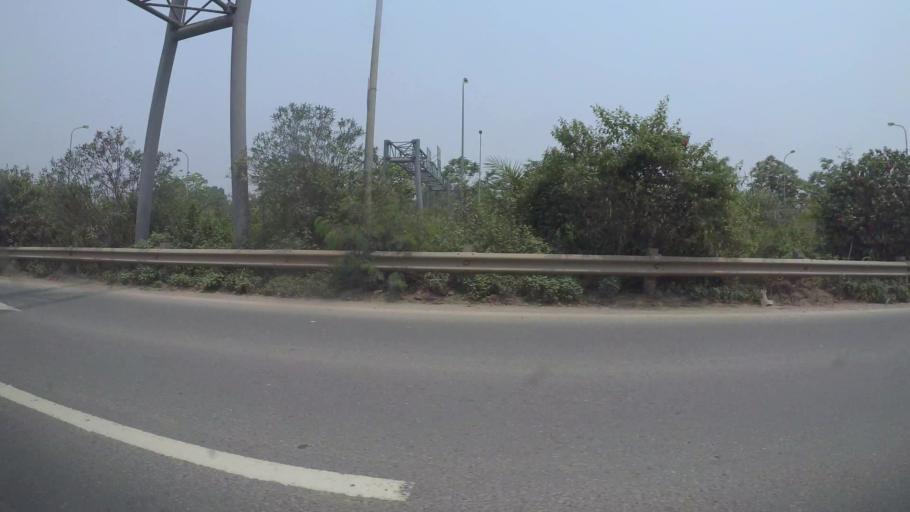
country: VN
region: Ha Noi
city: Lien Quan
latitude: 20.9902
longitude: 105.5337
